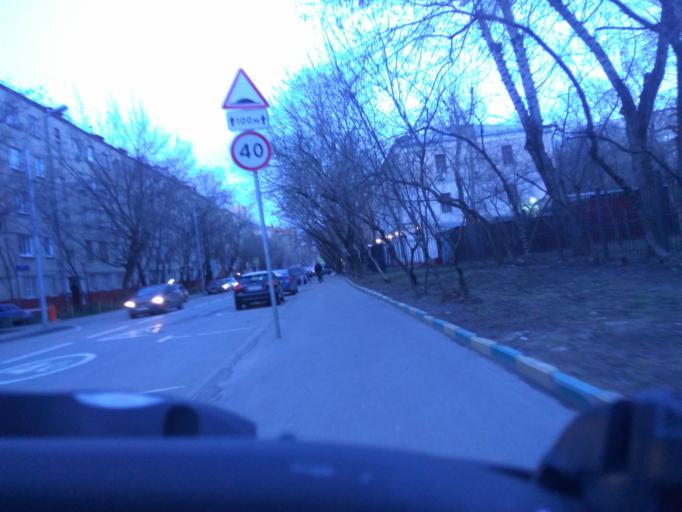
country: RU
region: Moskovskaya
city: Presnenskiy
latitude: 55.7406
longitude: 37.5444
